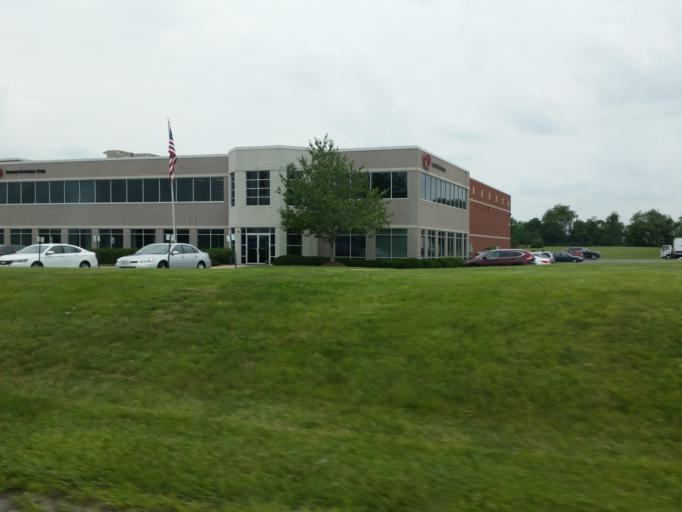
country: US
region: Pennsylvania
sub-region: York County
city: Emigsville
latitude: 40.0193
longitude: -76.7477
